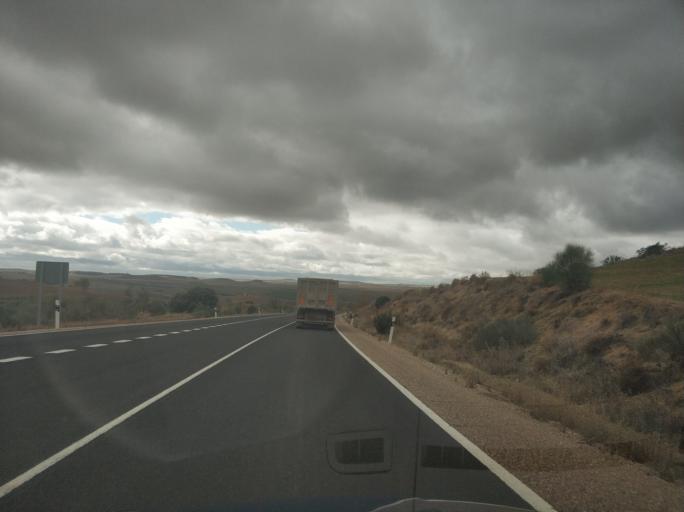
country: ES
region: Castille and Leon
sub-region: Provincia de Zamora
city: Castrillo de la Guarena
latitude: 41.2379
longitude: -5.2995
